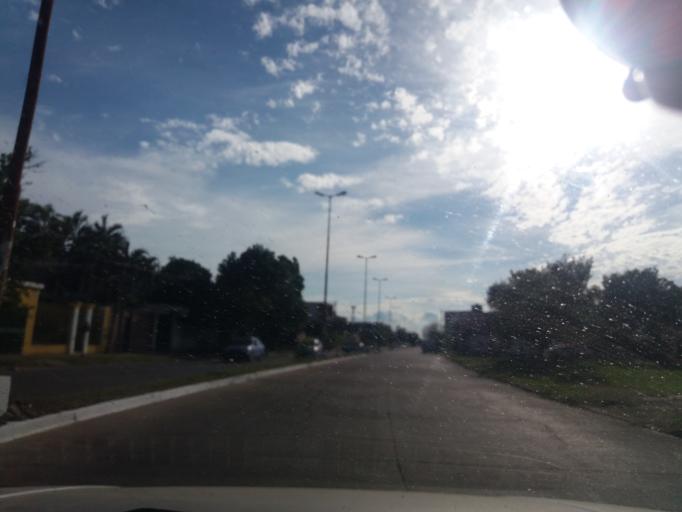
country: AR
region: Corrientes
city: Corrientes
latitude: -27.4857
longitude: -58.8345
